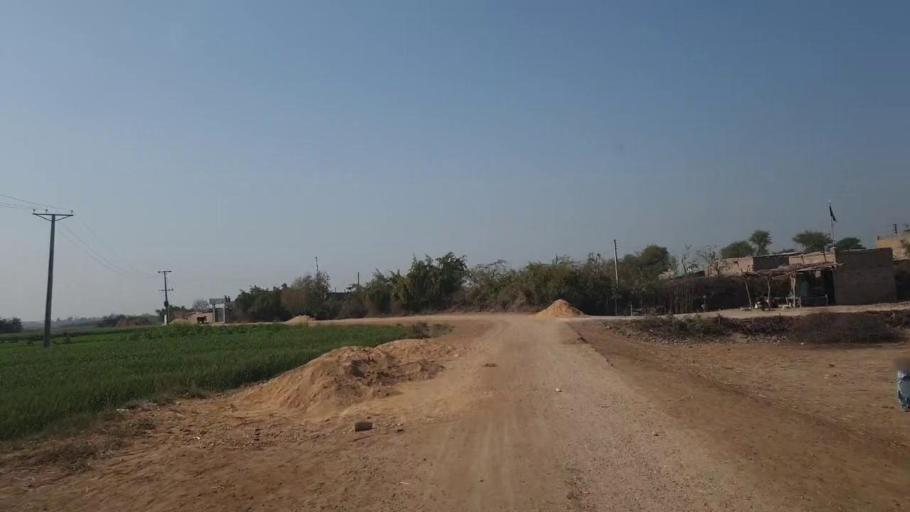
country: PK
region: Sindh
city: Shahdadpur
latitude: 26.0385
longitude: 68.4617
